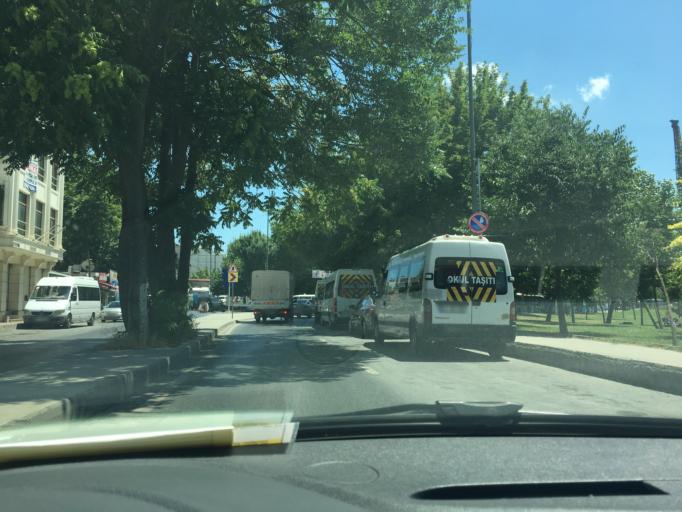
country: TR
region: Istanbul
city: Istanbul
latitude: 41.0409
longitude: 28.9503
